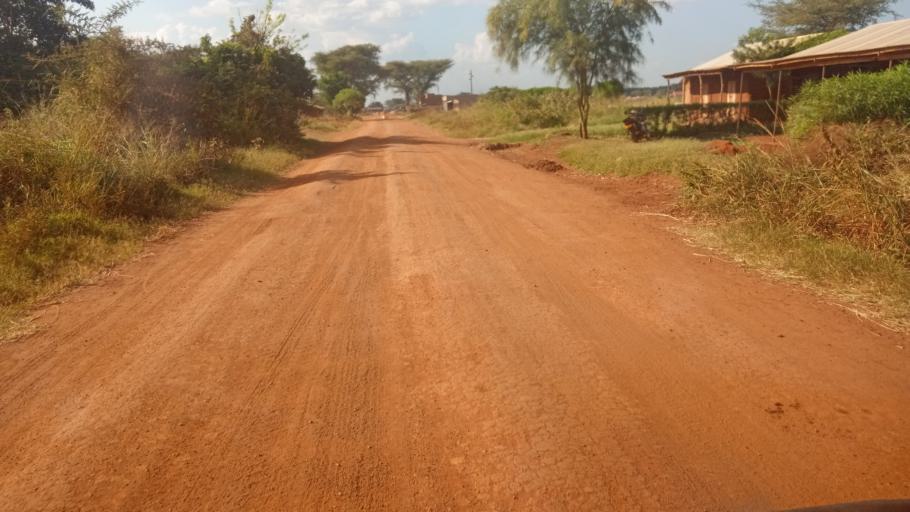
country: UG
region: Eastern Region
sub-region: Kween District
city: Binyin
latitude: 1.5216
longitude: 34.4916
